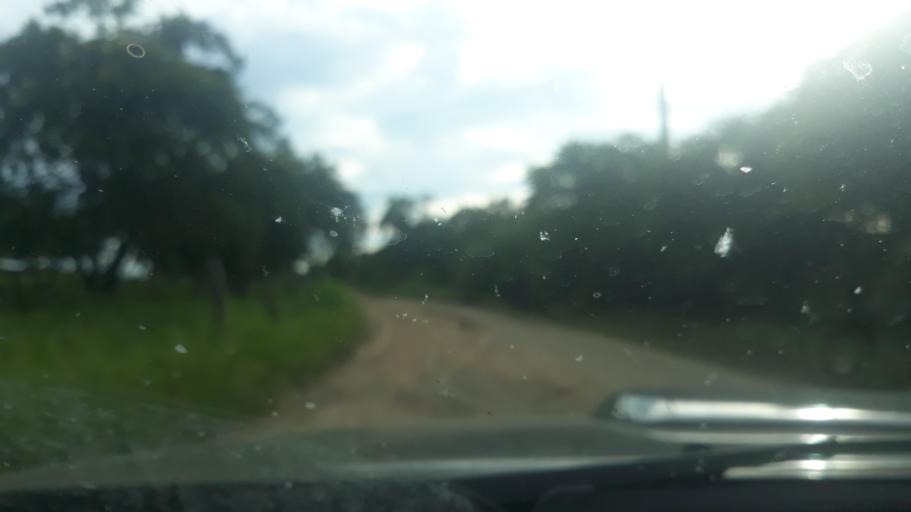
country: BR
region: Bahia
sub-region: Riacho De Santana
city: Riacho de Santana
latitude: -13.8874
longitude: -43.0238
